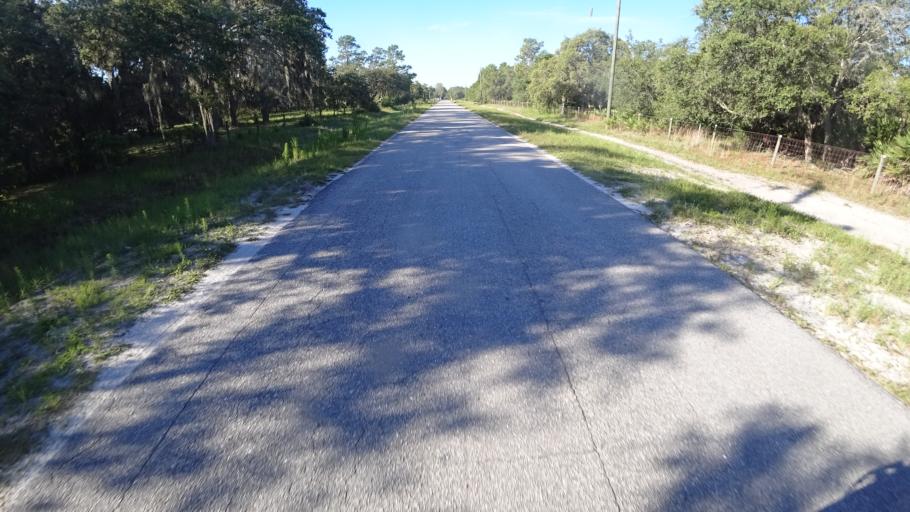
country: US
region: Florida
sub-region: Sarasota County
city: Fruitville
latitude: 27.4113
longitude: -82.2615
